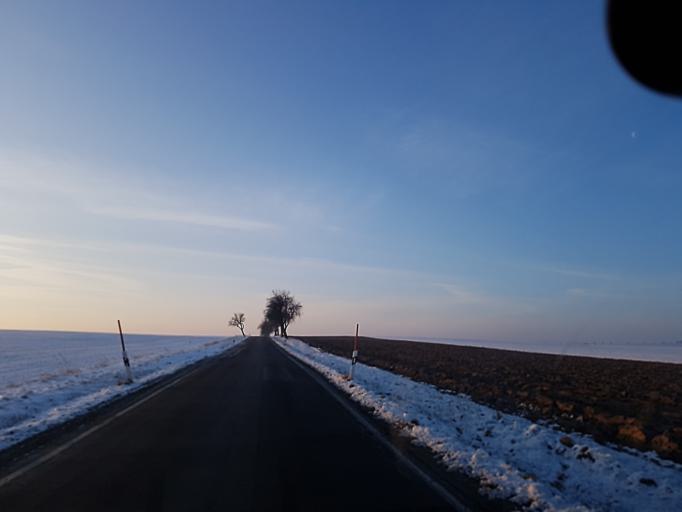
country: DE
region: Saxony
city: Grossweitzschen
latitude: 51.1900
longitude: 13.0325
